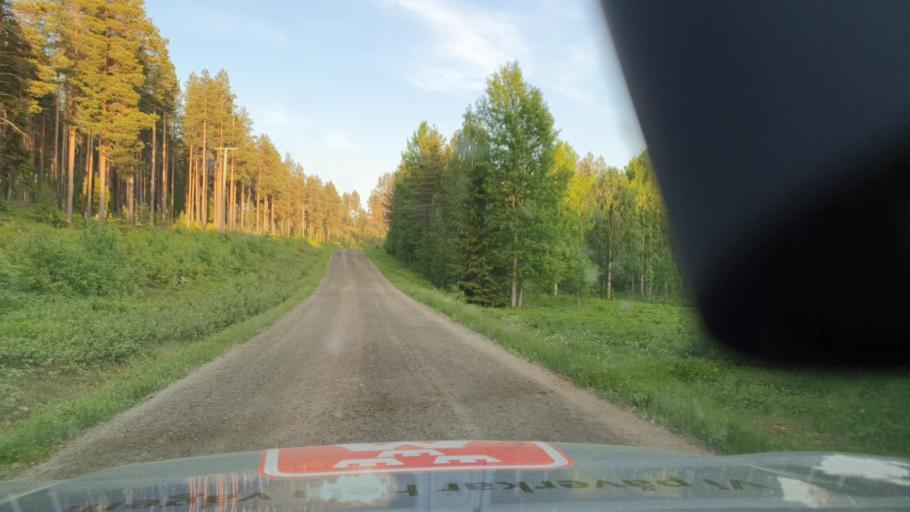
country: SE
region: Norrbotten
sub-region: Bodens Kommun
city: Boden
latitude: 66.1520
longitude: 21.5606
